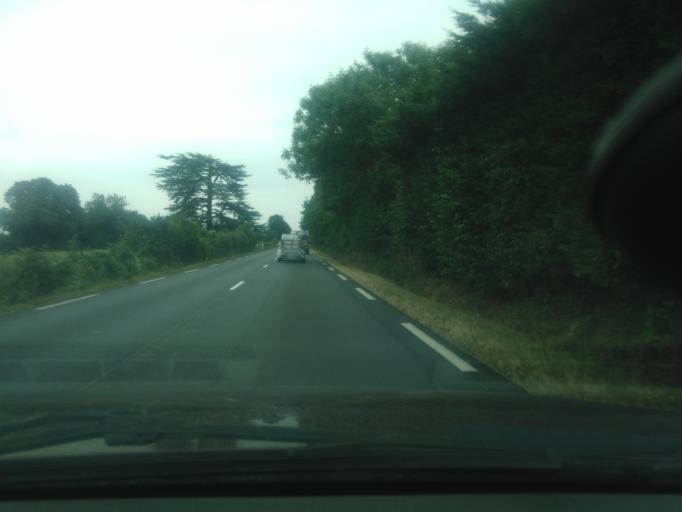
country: FR
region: Pays de la Loire
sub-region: Departement de la Vendee
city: Bazoges-en-Pareds
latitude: 46.6797
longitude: -0.9532
